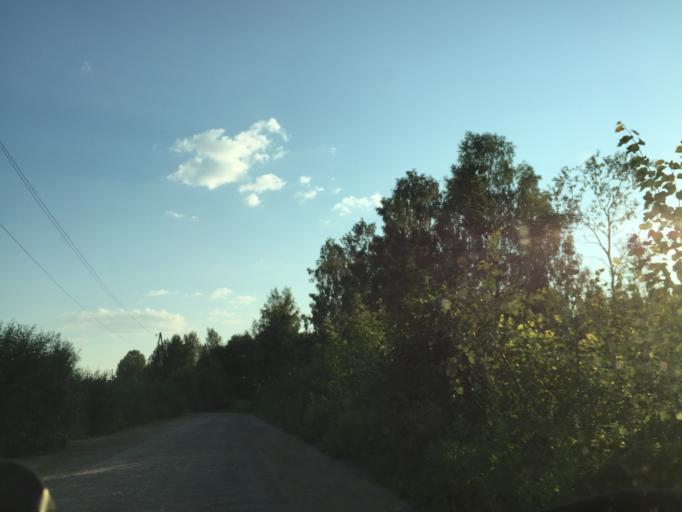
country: LV
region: Riga
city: Bergi
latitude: 56.9751
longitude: 24.3468
